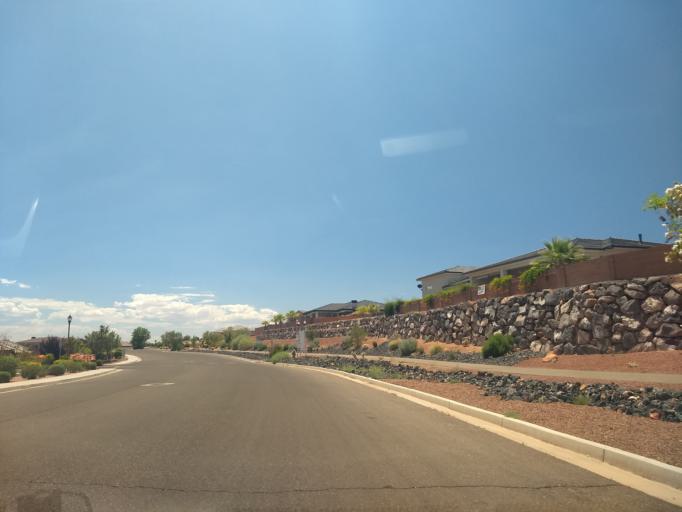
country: US
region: Utah
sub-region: Washington County
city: Washington
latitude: 37.1564
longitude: -113.5316
